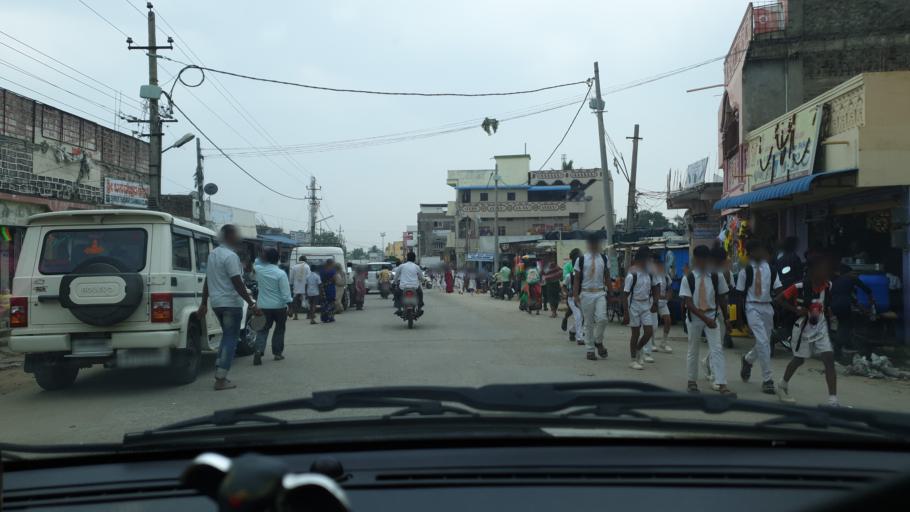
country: IN
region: Karnataka
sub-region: Yadgir
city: Gurmatkal
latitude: 16.8694
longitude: 77.3912
